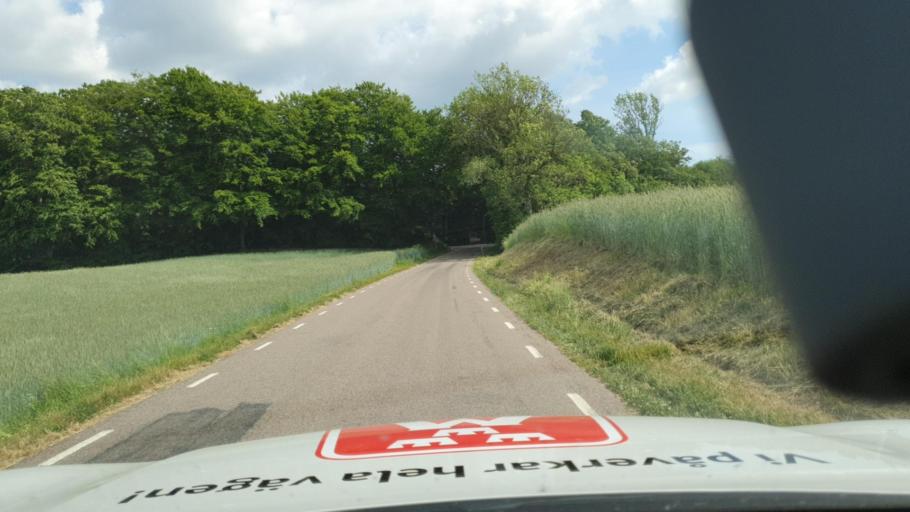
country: SE
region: Skane
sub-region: Skurups Kommun
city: Skurup
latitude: 55.5055
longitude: 13.4849
